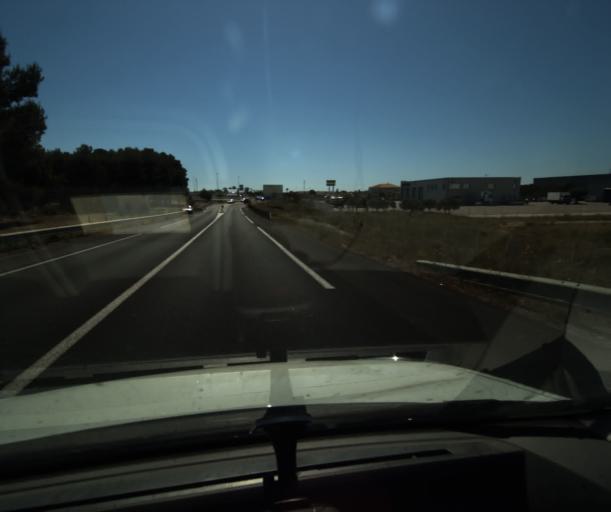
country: FR
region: Languedoc-Roussillon
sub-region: Departement des Pyrenees-Orientales
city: Rivesaltes
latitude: 42.7808
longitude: 2.8968
